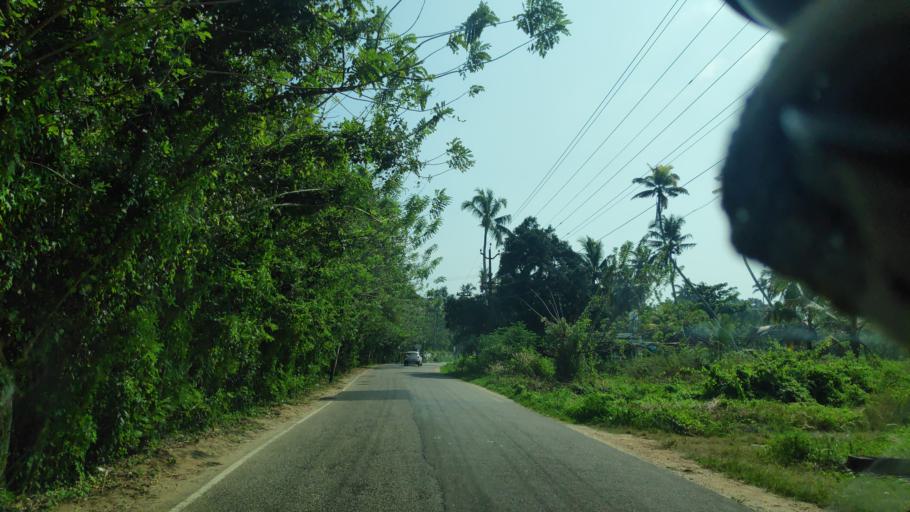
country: IN
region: Kerala
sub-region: Alappuzha
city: Shertallai
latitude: 9.6203
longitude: 76.3004
